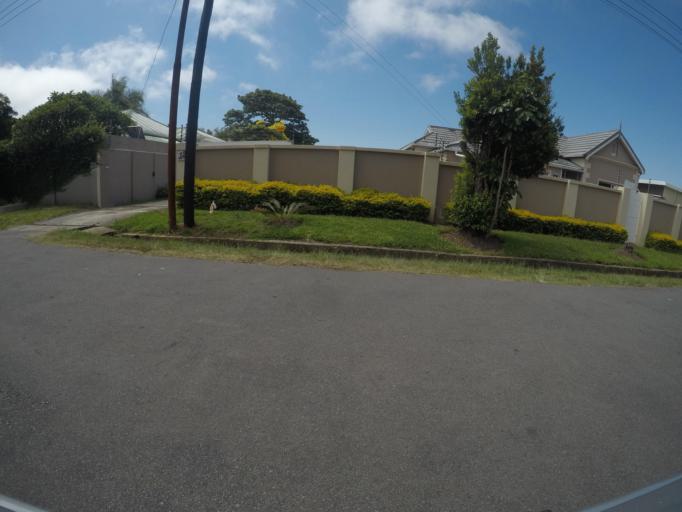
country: ZA
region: Eastern Cape
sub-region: Buffalo City Metropolitan Municipality
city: East London
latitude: -32.9759
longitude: 27.9013
